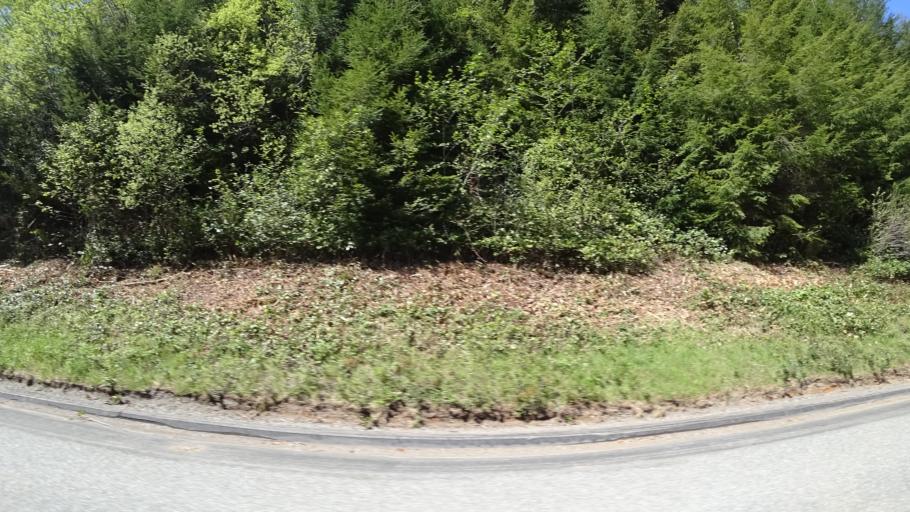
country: US
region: California
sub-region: Humboldt County
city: Westhaven-Moonstone
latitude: 41.4085
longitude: -124.0030
